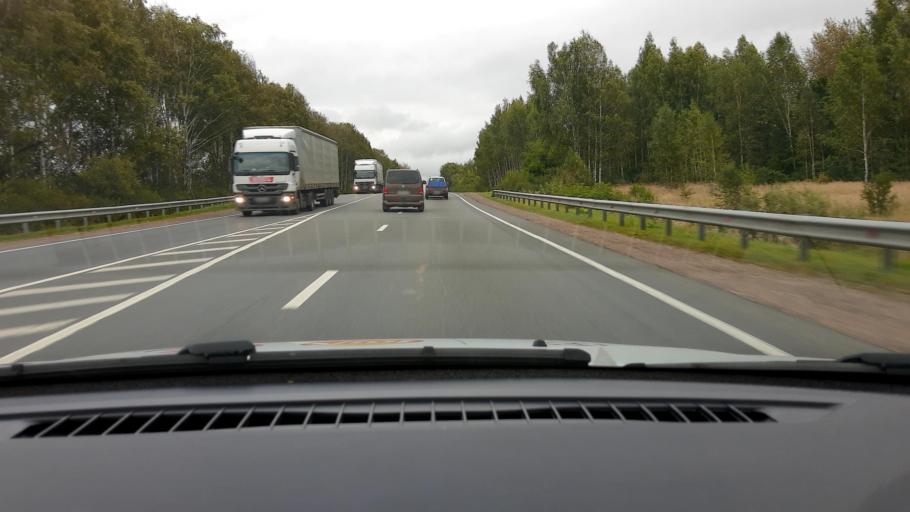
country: RU
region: Nizjnij Novgorod
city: Pamyat' Parizhskoy Kommuny
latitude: 56.0403
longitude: 44.4654
